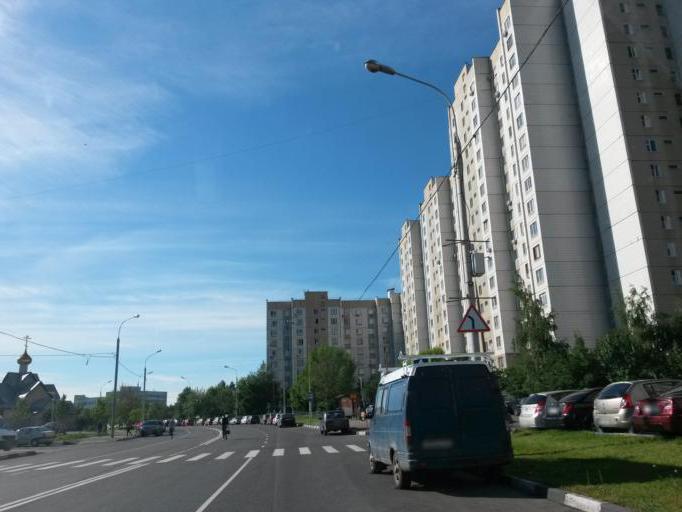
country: RU
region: Moscow
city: Brateyevo
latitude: 55.6322
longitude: 37.7633
